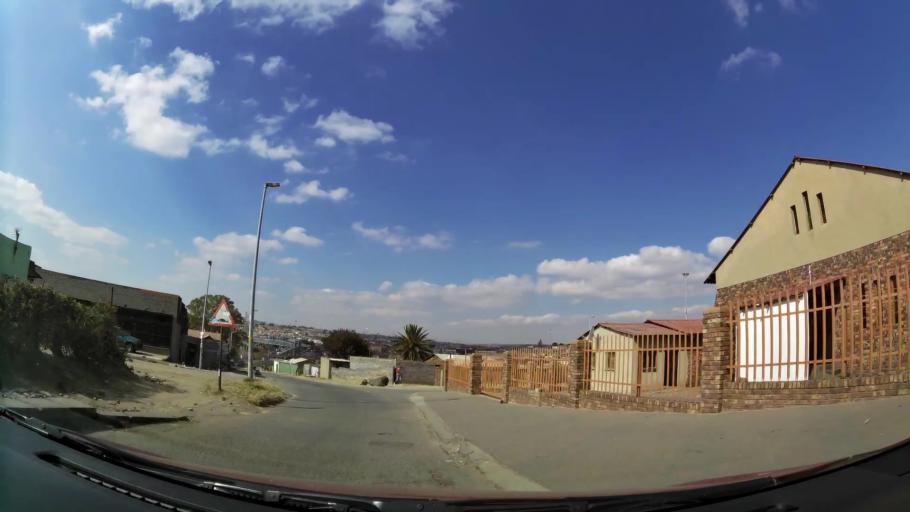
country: ZA
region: Gauteng
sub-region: Ekurhuleni Metropolitan Municipality
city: Tembisa
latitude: -26.0200
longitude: 28.1963
